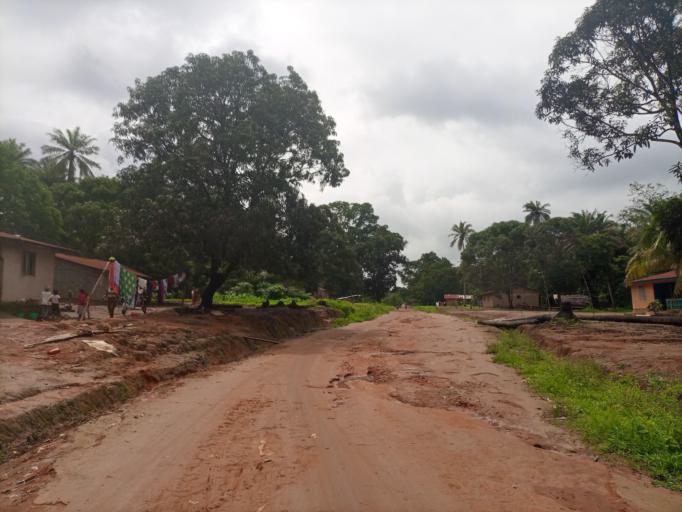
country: SL
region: Northern Province
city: Sawkta
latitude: 8.6363
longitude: -13.1966
